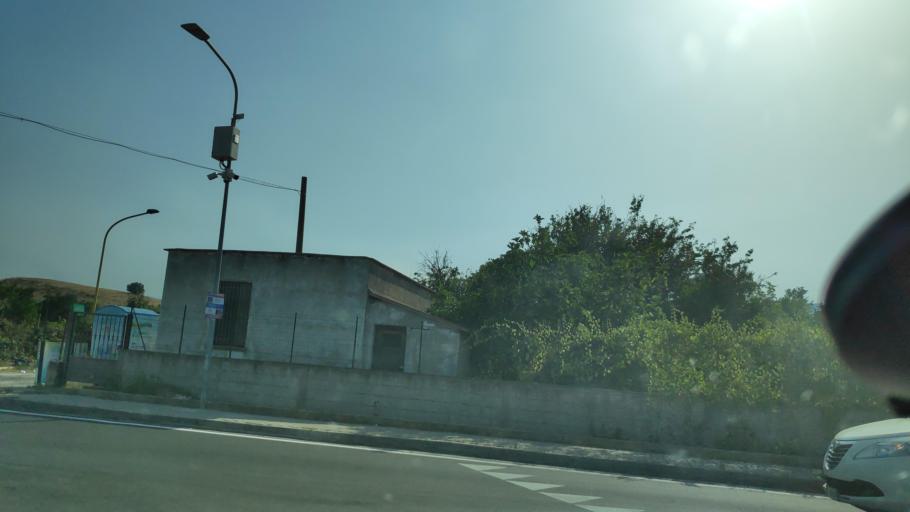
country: IT
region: Calabria
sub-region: Provincia di Catanzaro
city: Isca Marina
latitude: 38.6040
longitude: 16.5584
